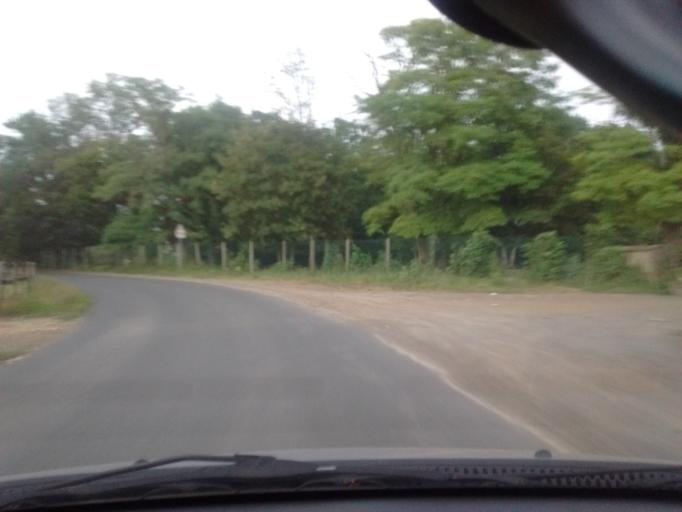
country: FR
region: Ile-de-France
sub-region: Departement de Seine-et-Marne
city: Pringy
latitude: 48.5169
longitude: 2.5482
